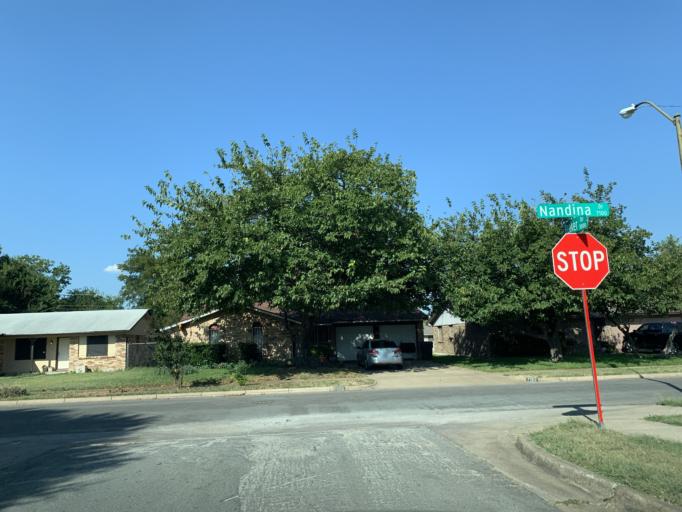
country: US
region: Texas
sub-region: Dallas County
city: Hutchins
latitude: 32.6592
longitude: -96.7713
